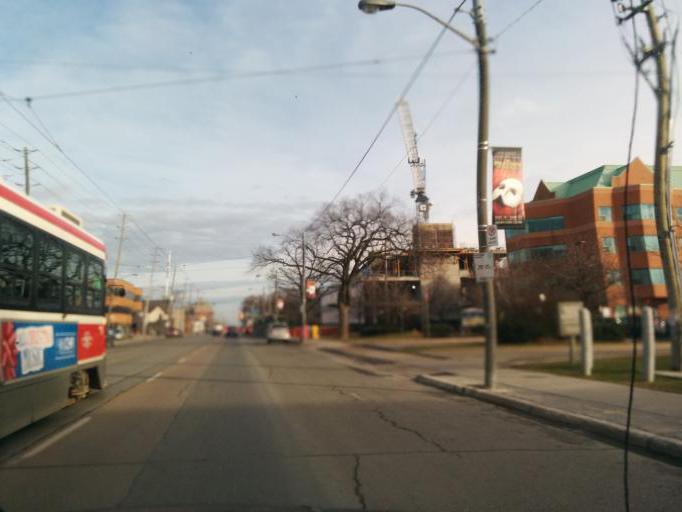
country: CA
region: Ontario
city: Etobicoke
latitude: 43.5976
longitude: -79.5196
